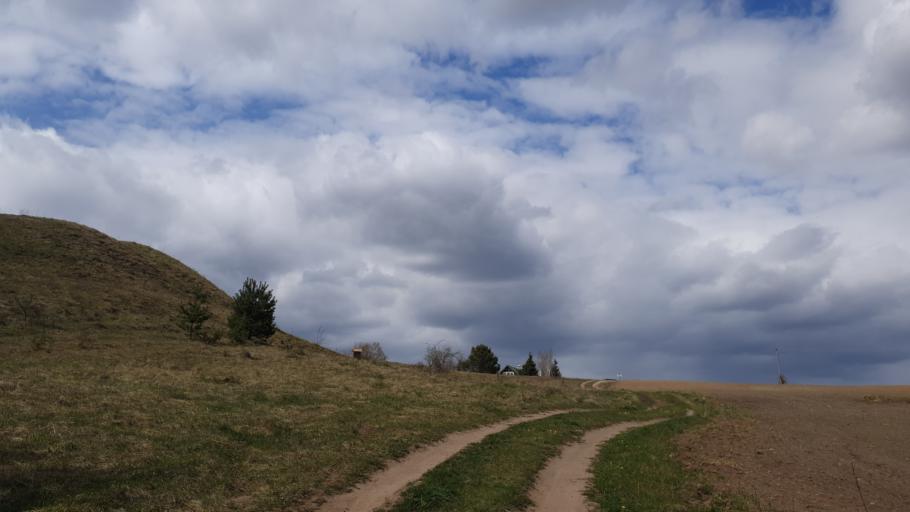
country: LT
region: Vilnius County
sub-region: Trakai
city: Rudiskes
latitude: 54.5094
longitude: 24.6833
